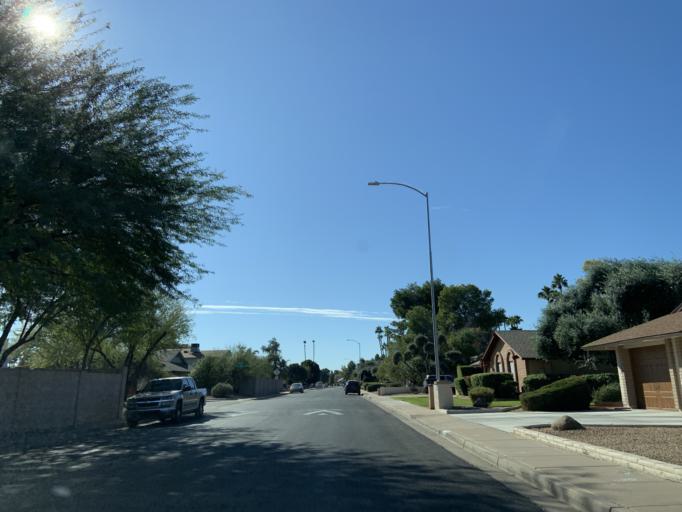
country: US
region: Arizona
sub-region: Maricopa County
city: San Carlos
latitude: 33.3737
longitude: -111.8649
